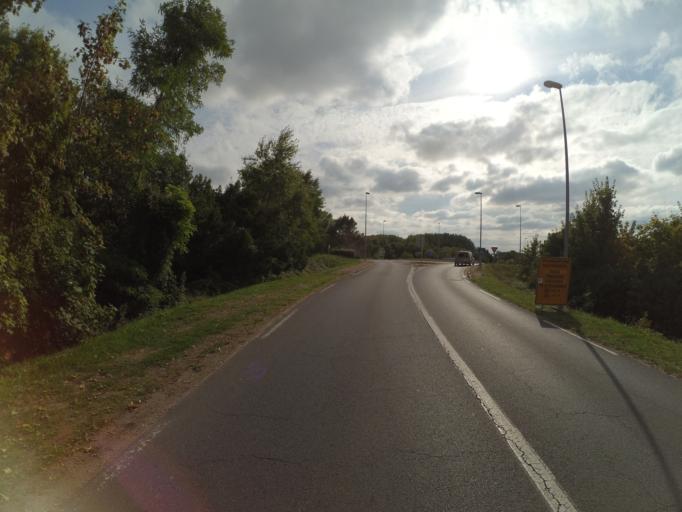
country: FR
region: Centre
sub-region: Departement d'Indre-et-Loire
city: Vernou-sur-Brenne
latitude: 47.4141
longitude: 0.8434
